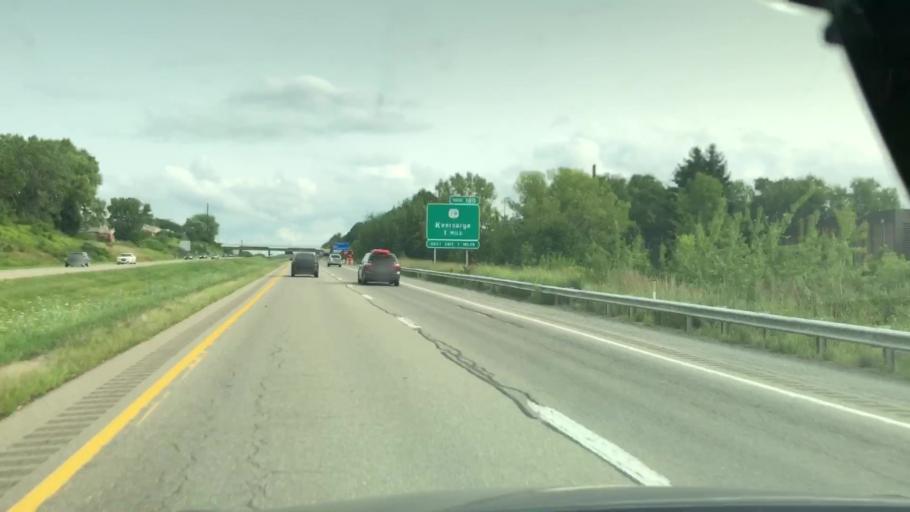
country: US
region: Pennsylvania
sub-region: Erie County
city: Erie
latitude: 42.0822
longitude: -80.1141
